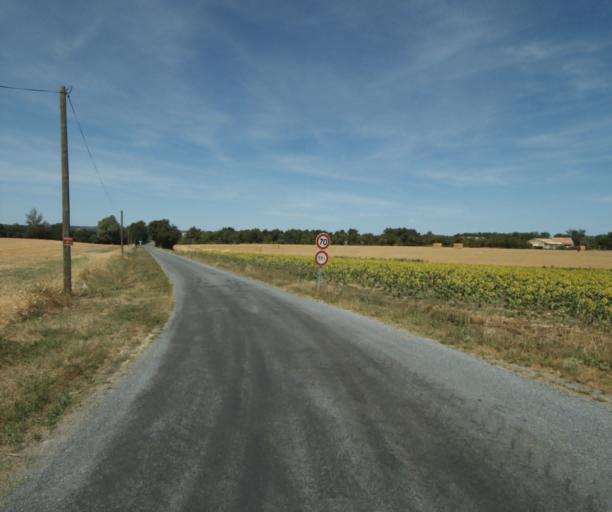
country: FR
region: Midi-Pyrenees
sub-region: Departement de la Haute-Garonne
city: Revel
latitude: 43.4958
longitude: 2.0047
